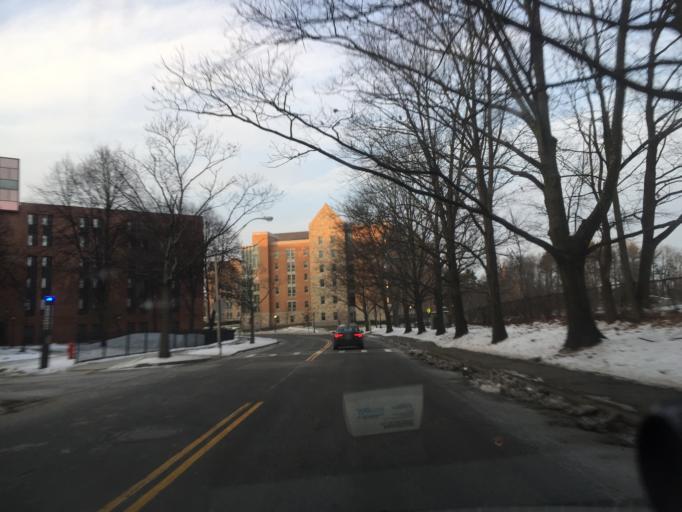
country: US
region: Massachusetts
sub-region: Middlesex County
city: Watertown
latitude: 42.3377
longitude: -71.1644
